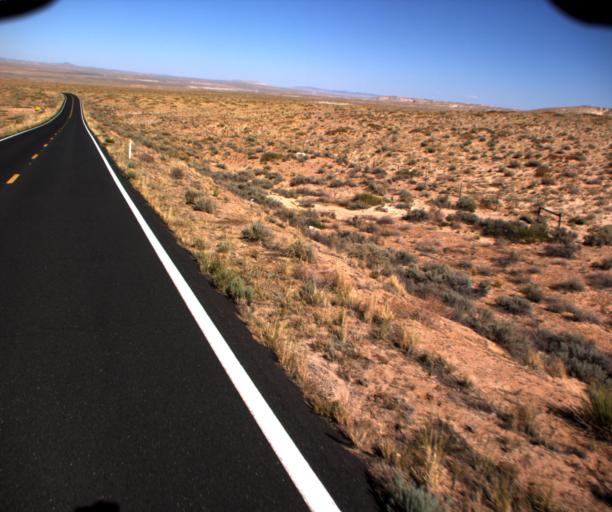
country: US
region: Arizona
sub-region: Coconino County
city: Tuba City
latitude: 36.0437
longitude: -111.1834
